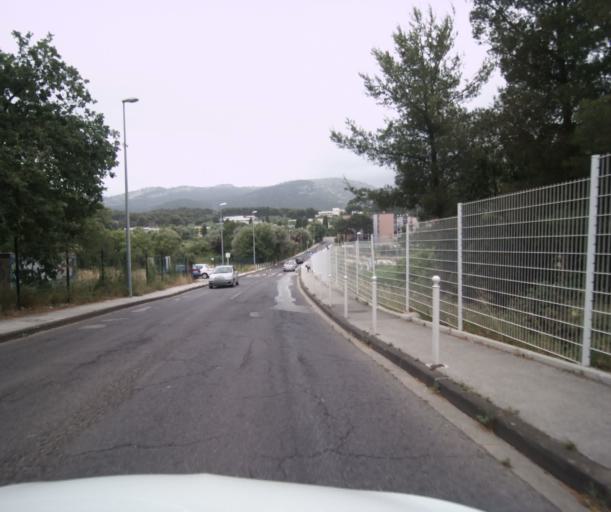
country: FR
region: Provence-Alpes-Cote d'Azur
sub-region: Departement du Var
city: Ollioules
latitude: 43.1374
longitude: 5.8830
